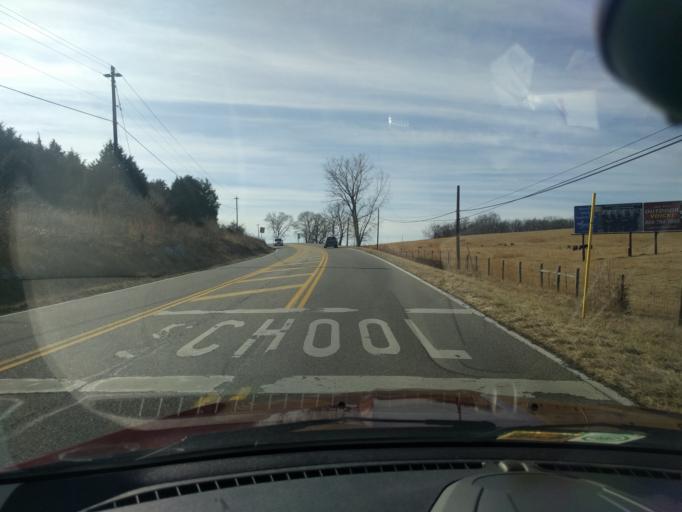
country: US
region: Virginia
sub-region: Augusta County
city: Verona
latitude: 38.2227
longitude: -78.9930
